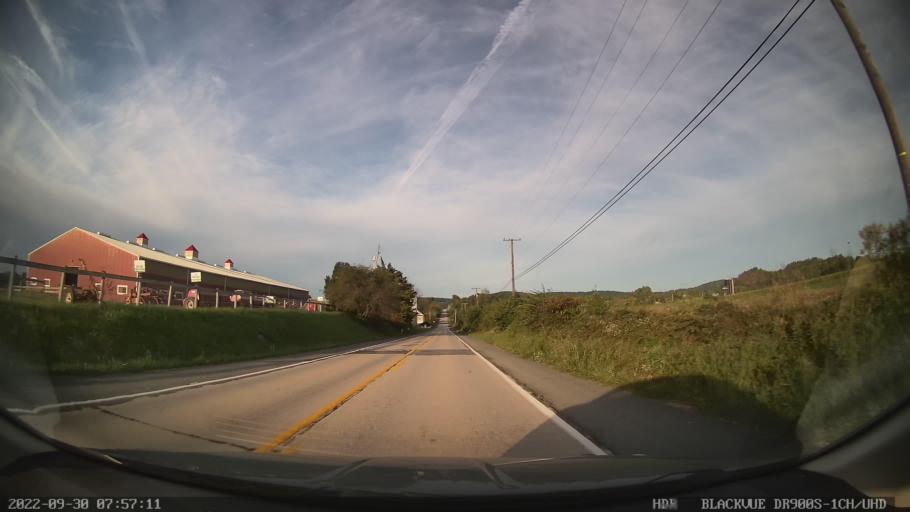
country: US
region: Pennsylvania
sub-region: Berks County
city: Oley
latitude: 40.3506
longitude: -75.7824
